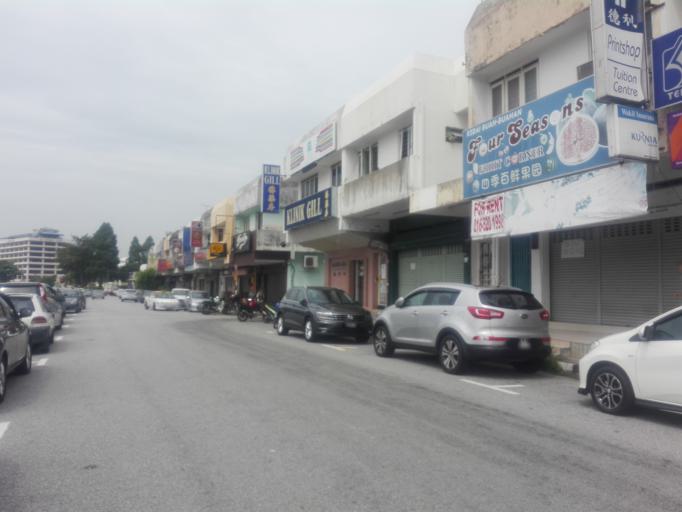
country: MY
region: Perak
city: Ipoh
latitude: 4.6077
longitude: 101.1200
